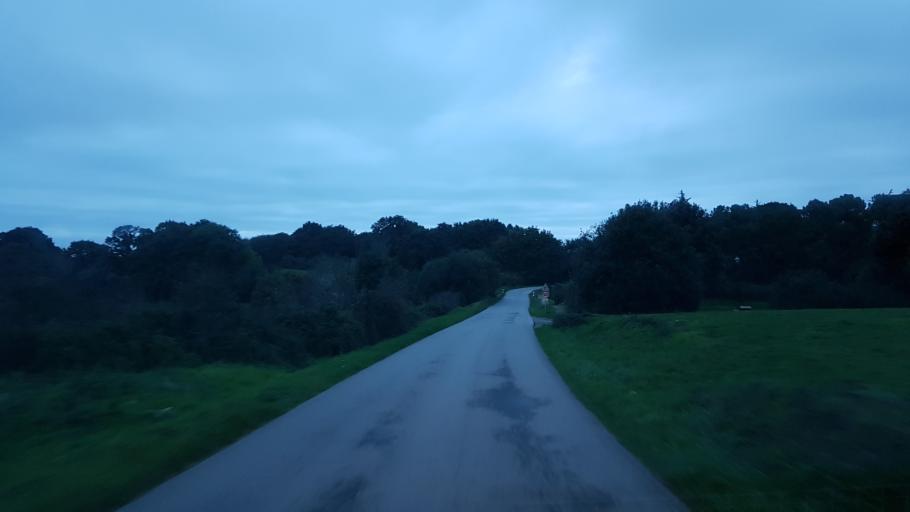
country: FR
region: Brittany
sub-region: Departement du Morbihan
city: Sarzeau
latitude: 47.5374
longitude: -2.7975
